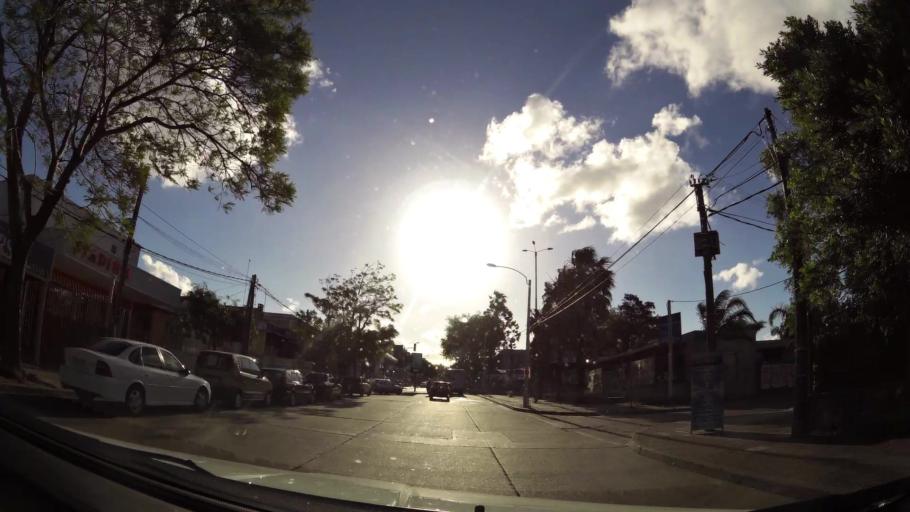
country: UY
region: Montevideo
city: Montevideo
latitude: -34.8738
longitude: -56.2485
